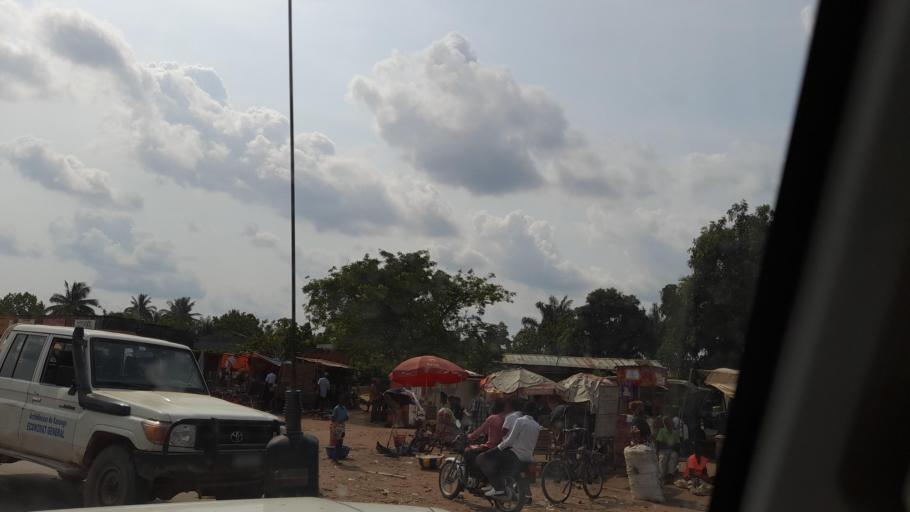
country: CD
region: Kasai-Occidental
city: Kananga
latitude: -5.8972
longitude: 22.4560
